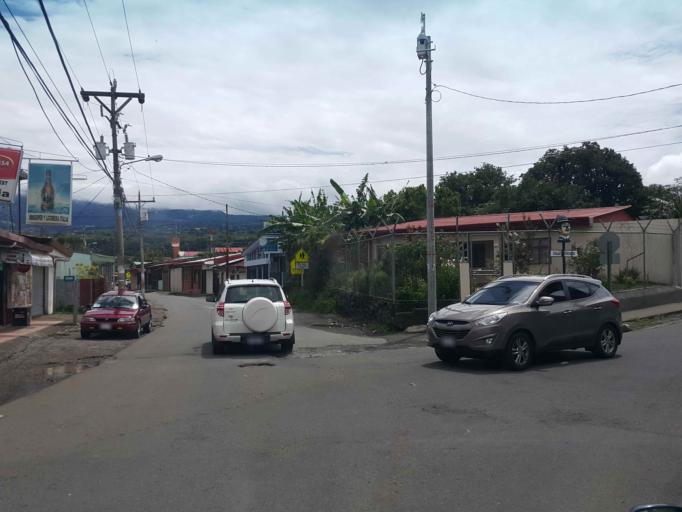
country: CR
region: Heredia
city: Heredia
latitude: 10.0119
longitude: -84.1182
